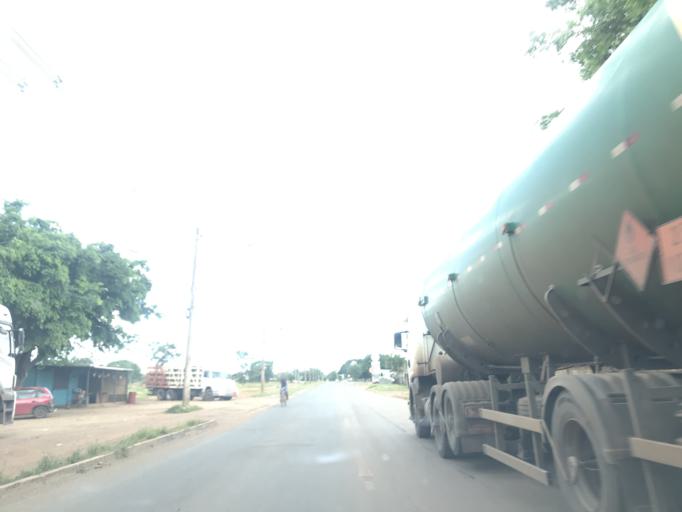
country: BR
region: Federal District
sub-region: Brasilia
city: Brasilia
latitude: -15.7965
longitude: -47.9752
